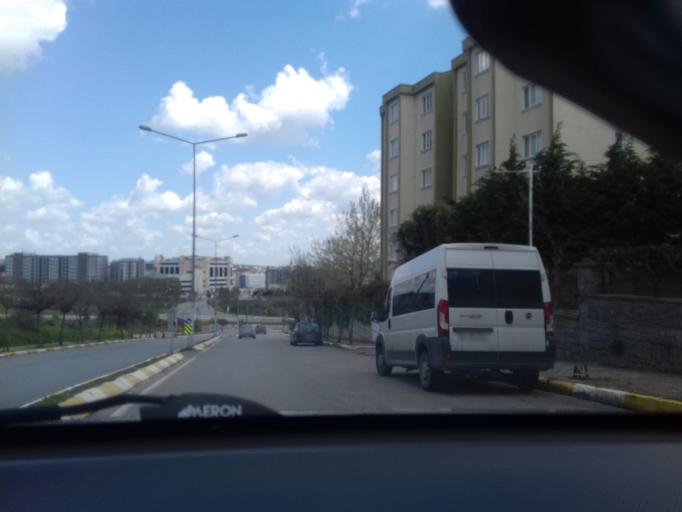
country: TR
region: Istanbul
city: Sultanbeyli
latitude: 40.9201
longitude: 29.2833
